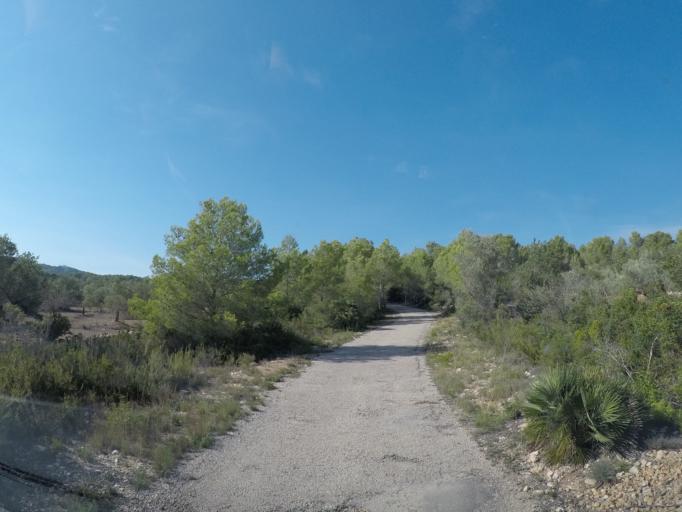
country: ES
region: Catalonia
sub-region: Provincia de Tarragona
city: El Perello
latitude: 40.9099
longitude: 0.7245
